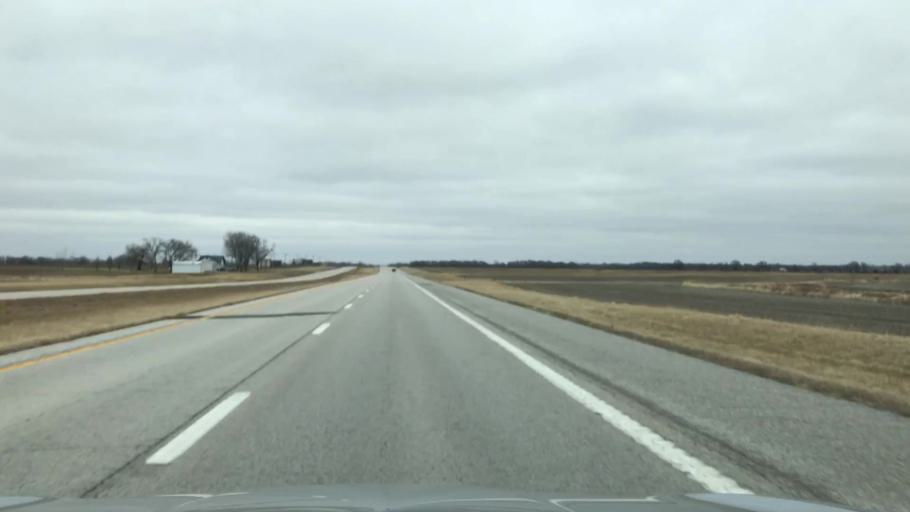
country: US
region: Missouri
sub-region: Livingston County
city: Chillicothe
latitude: 39.7763
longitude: -93.4675
